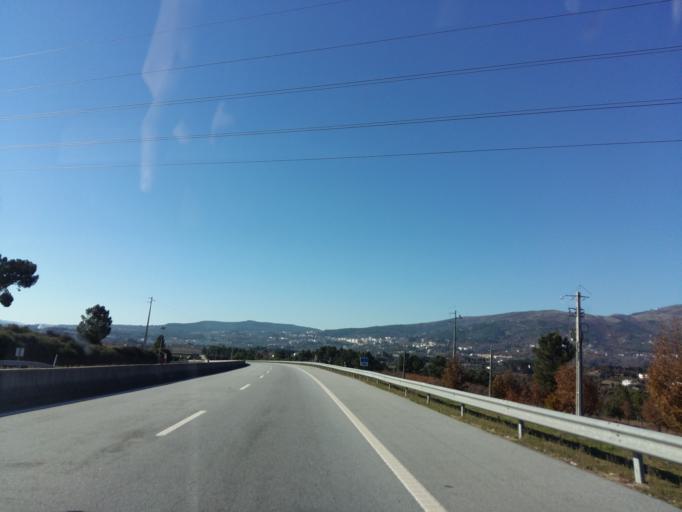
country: PT
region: Castelo Branco
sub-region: Covilha
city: Covilha
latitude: 40.2436
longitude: -7.4728
